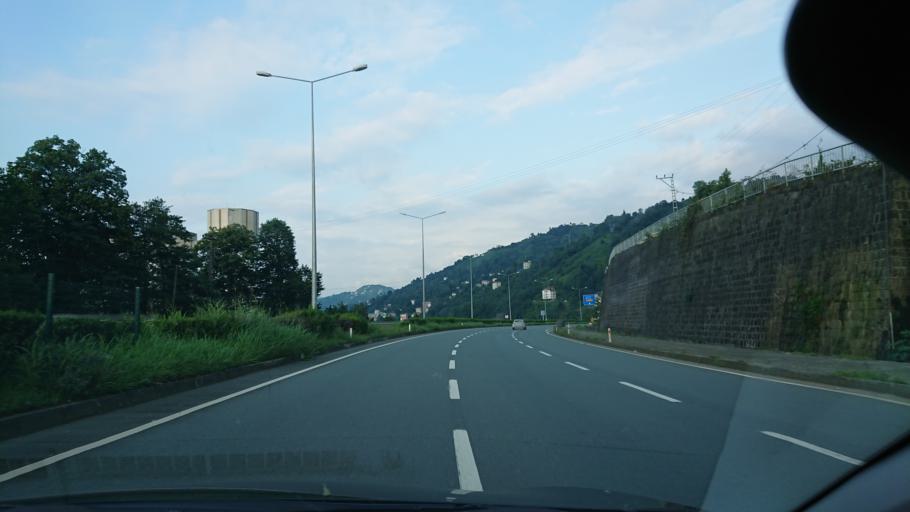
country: TR
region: Rize
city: Cayeli
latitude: 41.0769
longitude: 40.6791
